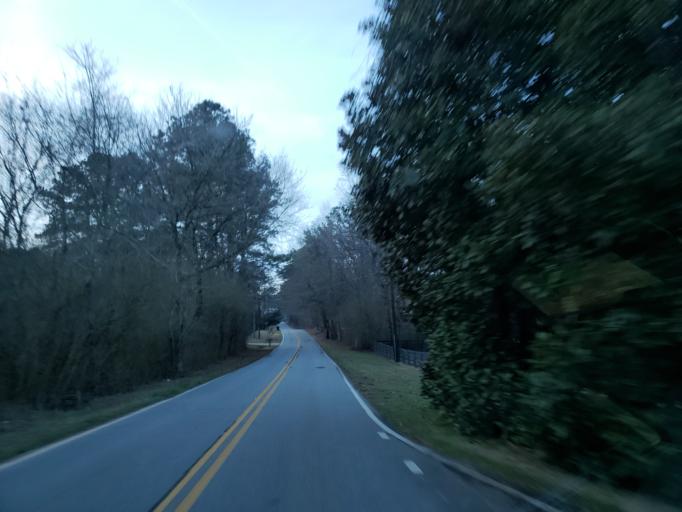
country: US
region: Georgia
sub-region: Cherokee County
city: Ball Ground
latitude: 34.2525
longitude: -84.3386
